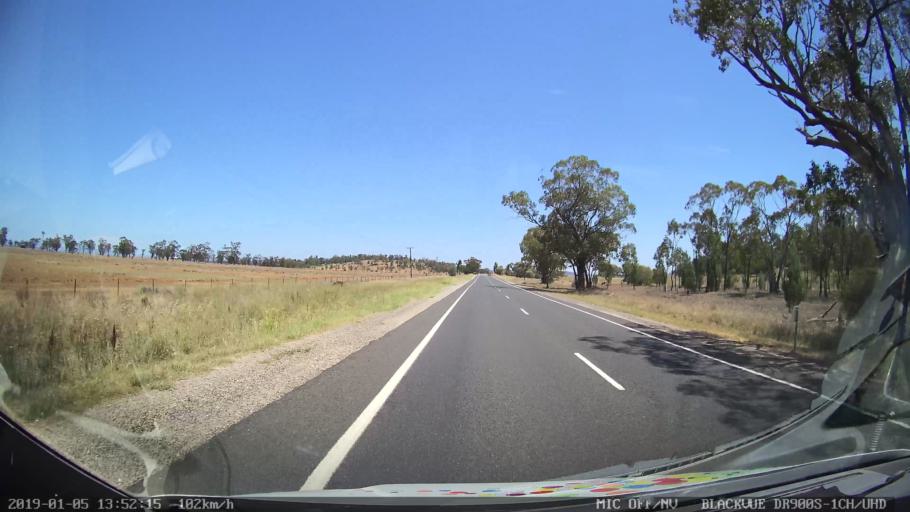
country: AU
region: New South Wales
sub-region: Gunnedah
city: Gunnedah
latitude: -31.0569
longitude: 150.2778
